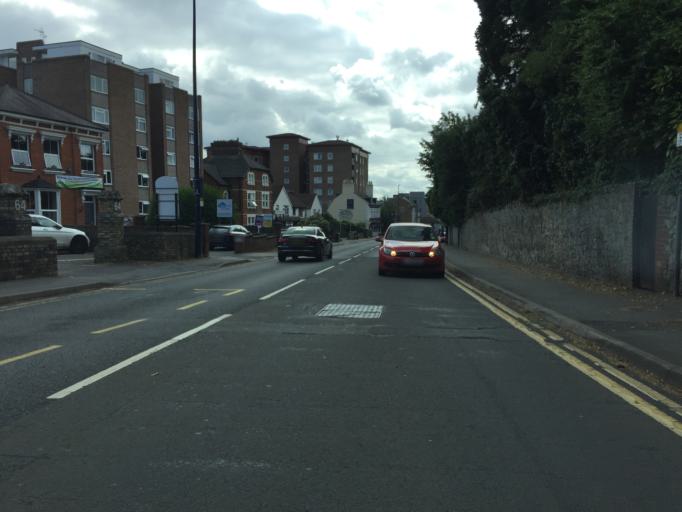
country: GB
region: England
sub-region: Kent
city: Maidstone
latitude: 51.2746
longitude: 0.5107
